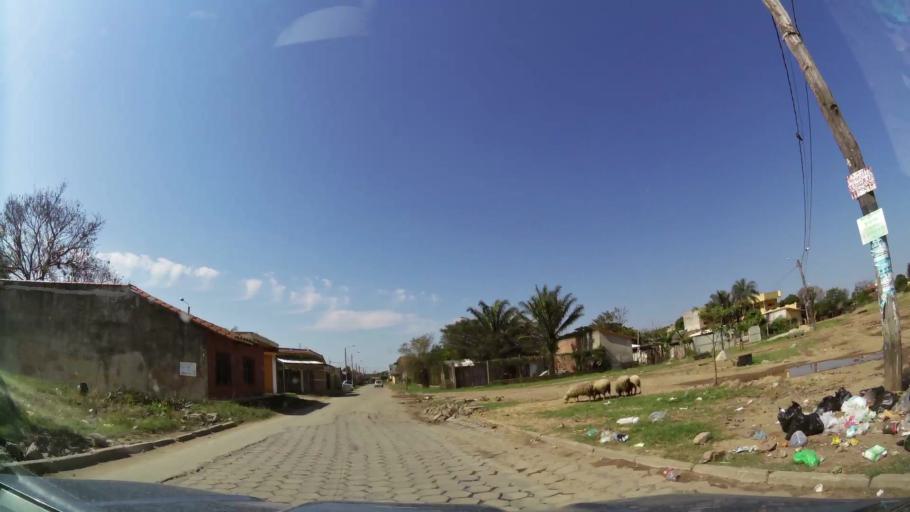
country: BO
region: Santa Cruz
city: Santa Cruz de la Sierra
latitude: -17.7596
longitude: -63.1188
